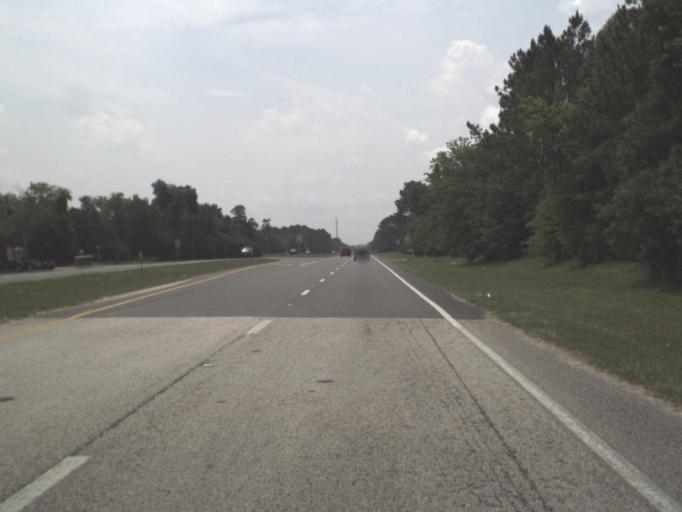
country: US
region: Florida
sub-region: Clay County
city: Green Cove Springs
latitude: 29.9055
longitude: -81.6760
